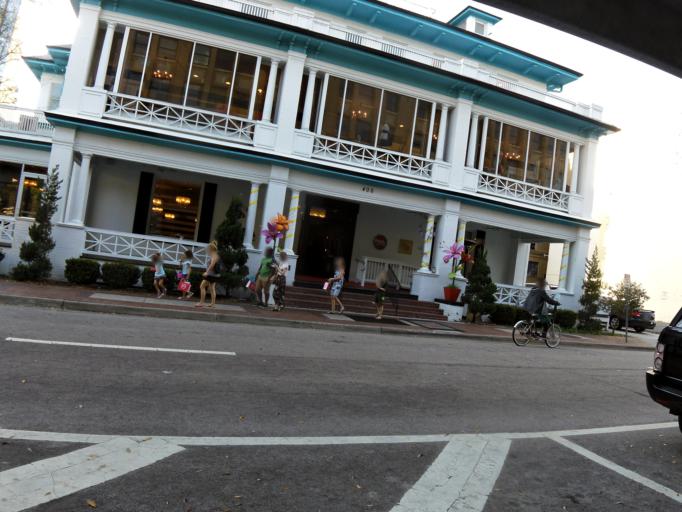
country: US
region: Florida
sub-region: Duval County
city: Jacksonville
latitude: 30.3299
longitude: -81.6597
